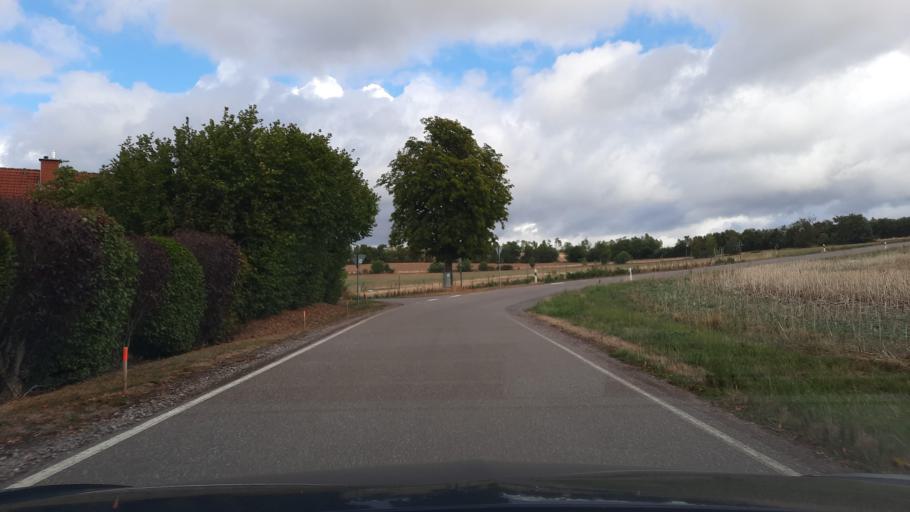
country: DE
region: Rheinland-Pfalz
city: Baldringen
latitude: 49.6132
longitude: 6.6637
